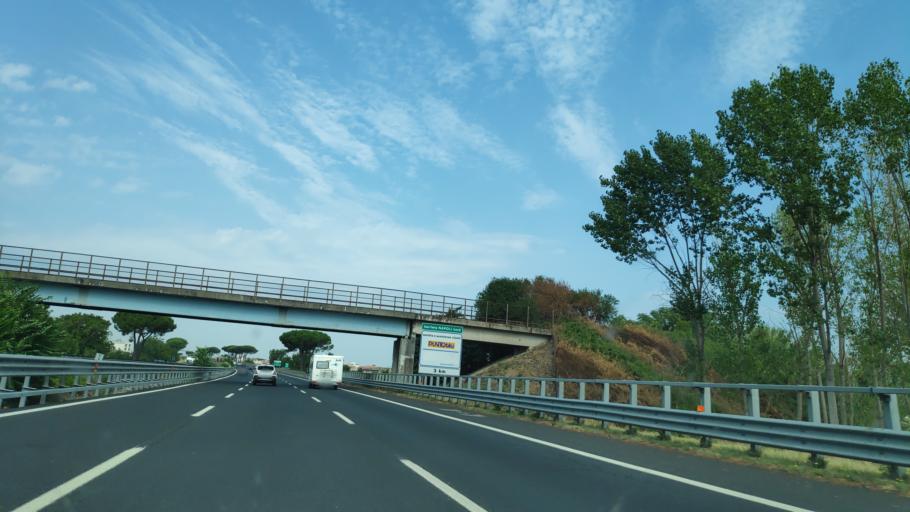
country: IT
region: Campania
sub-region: Provincia di Caserta
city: San Marco Evangelista
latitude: 41.0289
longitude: 14.3507
